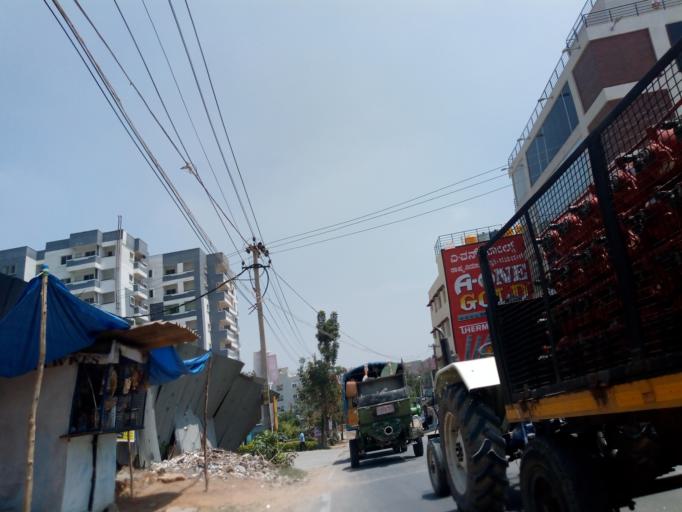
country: IN
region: Karnataka
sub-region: Bangalore Urban
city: Bangalore
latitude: 12.8847
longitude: 77.6558
